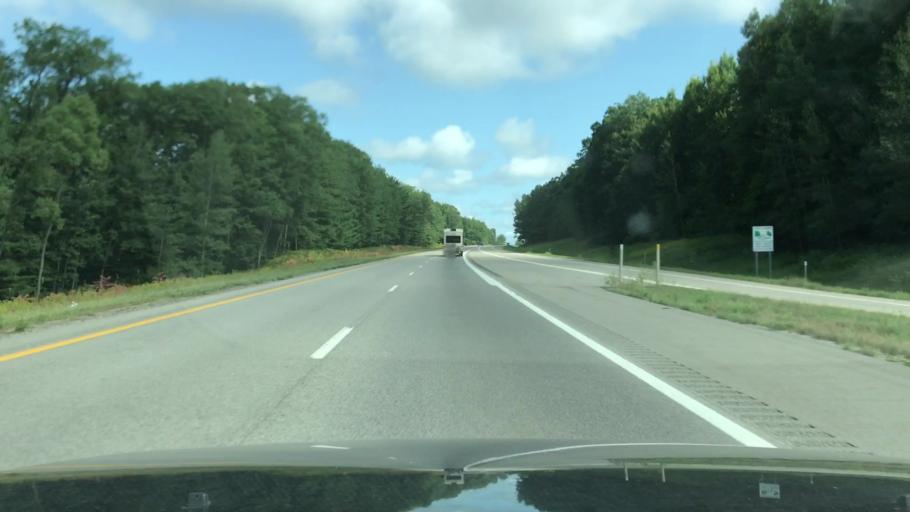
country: US
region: Michigan
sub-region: Montcalm County
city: Howard City
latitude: 43.4940
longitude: -85.4853
